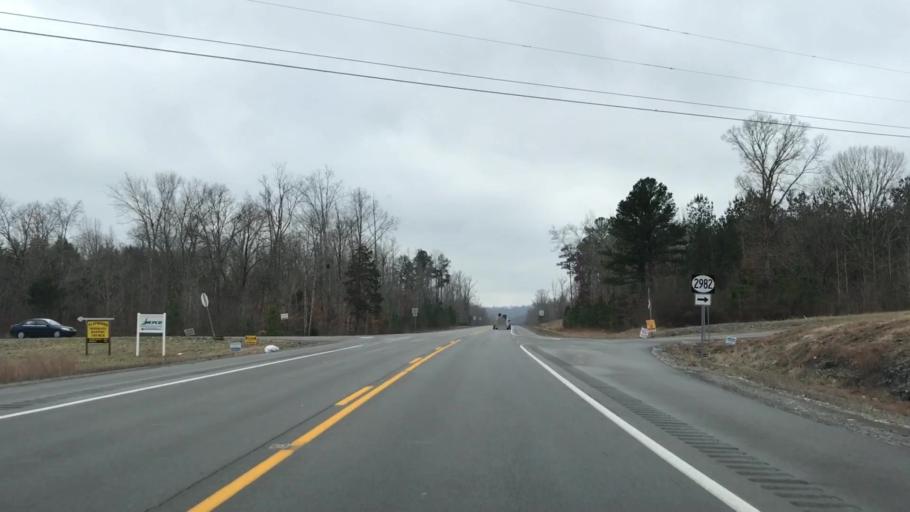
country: US
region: Kentucky
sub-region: Adair County
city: Columbia
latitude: 37.0493
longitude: -85.3635
